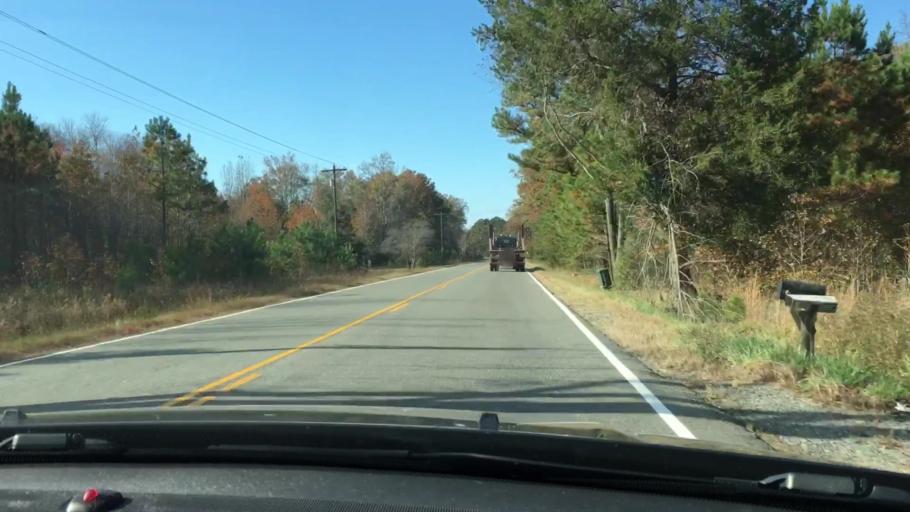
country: US
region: Virginia
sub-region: Hanover County
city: Hanover
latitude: 37.8230
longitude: -77.3266
